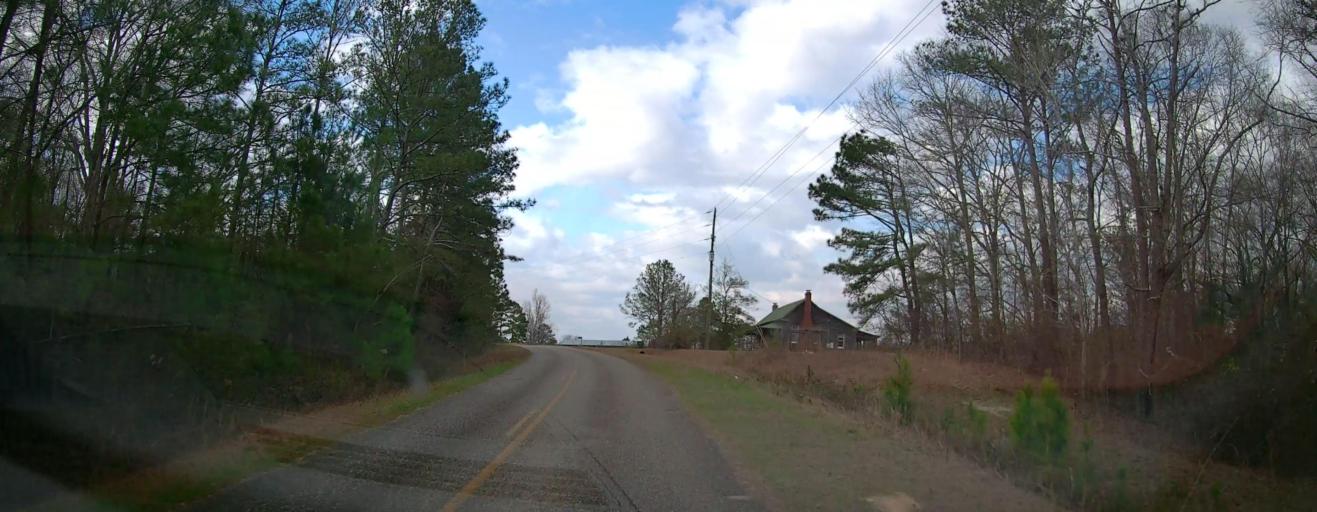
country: US
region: Georgia
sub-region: Marion County
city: Buena Vista
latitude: 32.4286
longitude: -84.4193
